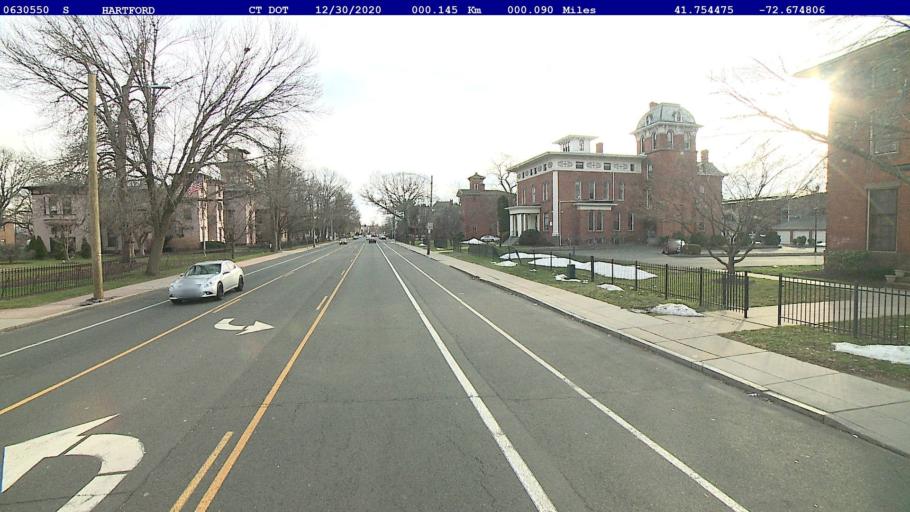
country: US
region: Connecticut
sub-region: Hartford County
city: Hartford
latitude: 41.7545
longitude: -72.6748
